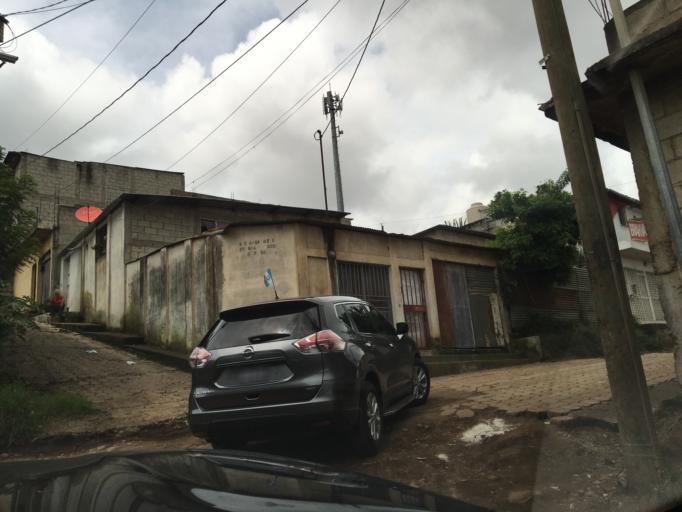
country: GT
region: Guatemala
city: Amatitlan
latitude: 14.4990
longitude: -90.5931
